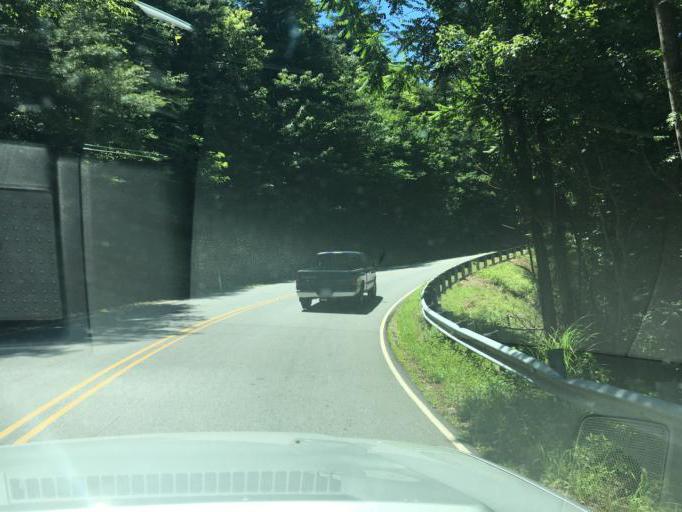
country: US
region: North Carolina
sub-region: Polk County
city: Tryon
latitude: 35.2311
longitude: -82.3330
